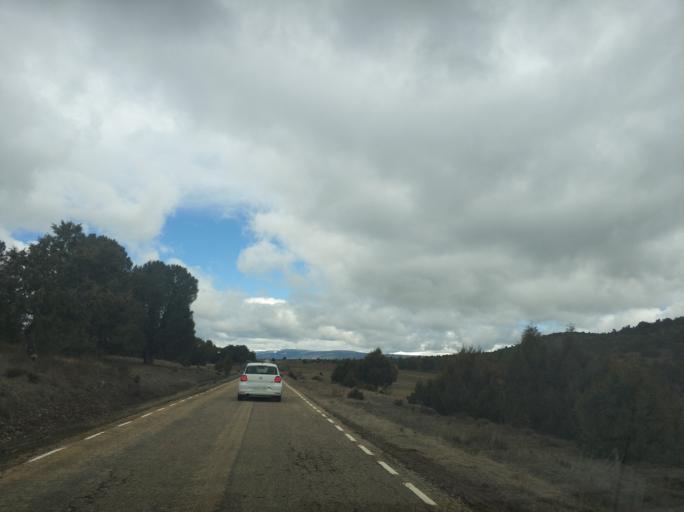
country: ES
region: Castille and Leon
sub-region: Provincia de Soria
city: Abejar
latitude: 41.7897
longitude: -2.7686
